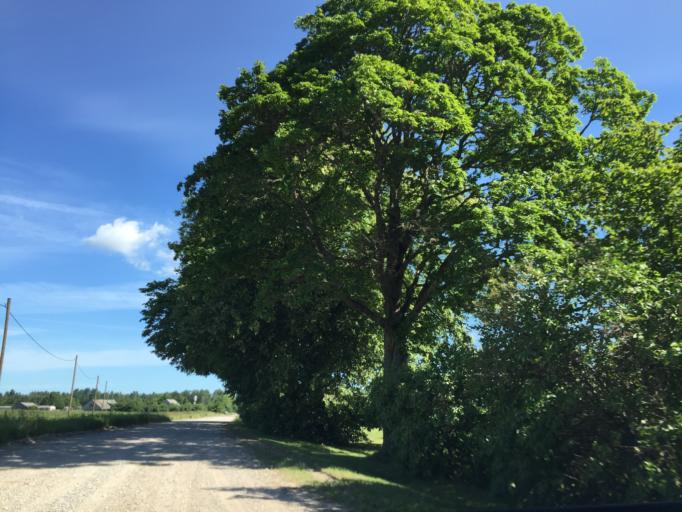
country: LV
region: Dundaga
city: Dundaga
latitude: 57.3487
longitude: 22.0258
